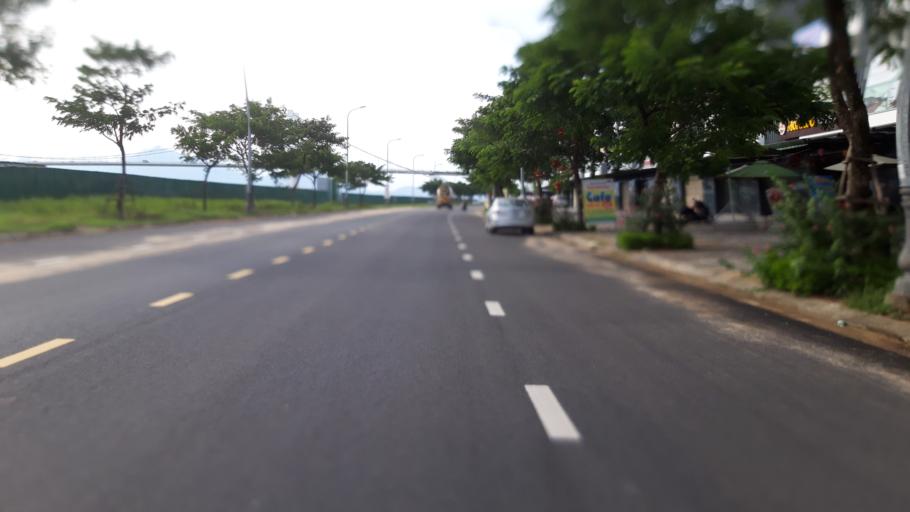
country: VN
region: Da Nang
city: Da Nang
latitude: 16.0915
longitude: 108.2262
